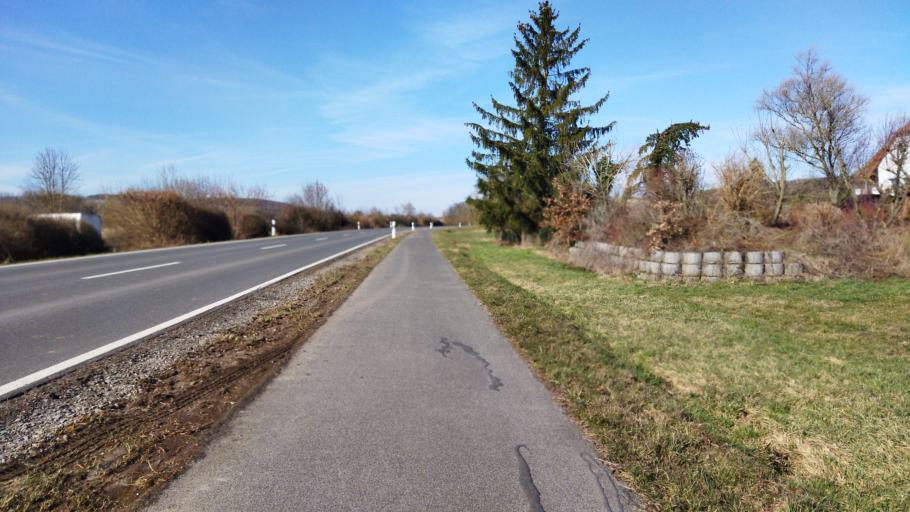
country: DE
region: Bavaria
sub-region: Regierungsbezirk Unterfranken
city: Wipfeld
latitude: 49.9085
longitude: 10.1895
